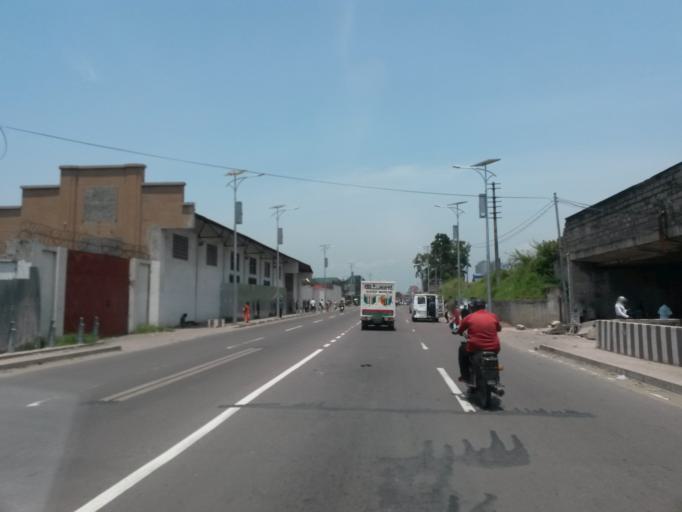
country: CD
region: Kinshasa
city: Kinshasa
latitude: -4.3053
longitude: 15.3263
